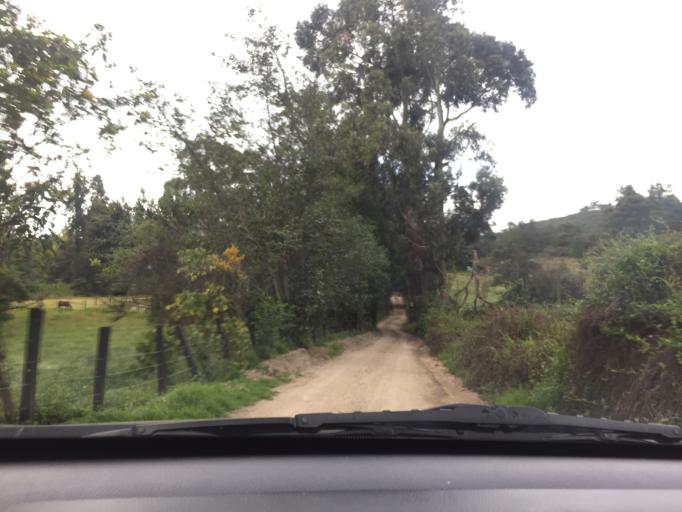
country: CO
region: Cundinamarca
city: Tabio
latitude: 4.9448
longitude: -74.1293
